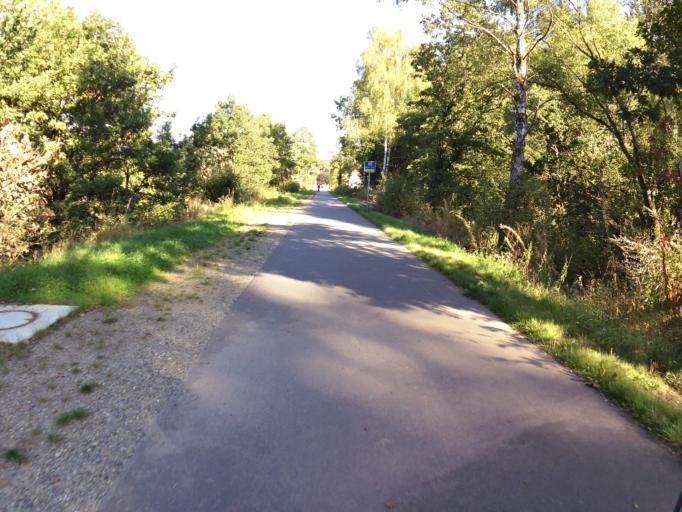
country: BE
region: Wallonia
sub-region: Province de Liege
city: Saint-Vith
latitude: 50.3297
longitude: 6.1192
